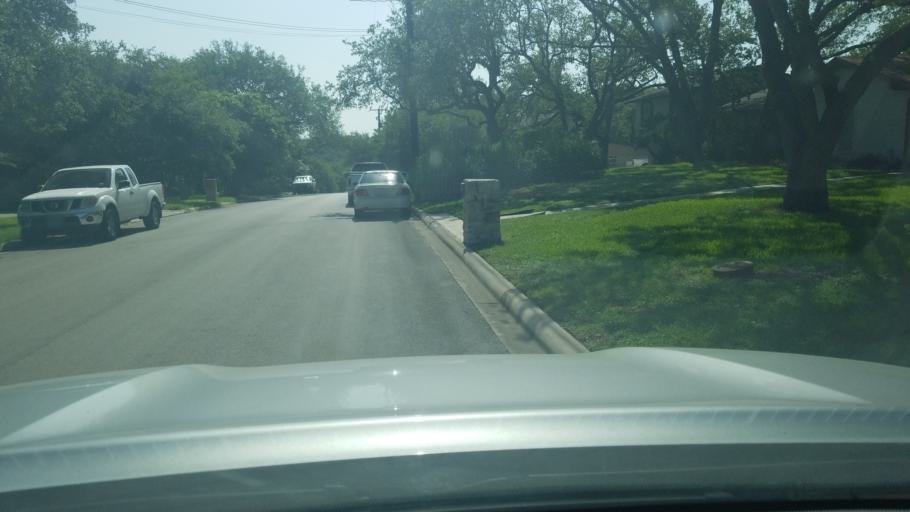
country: US
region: Texas
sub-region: Bexar County
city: Hollywood Park
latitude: 29.6037
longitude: -98.4838
